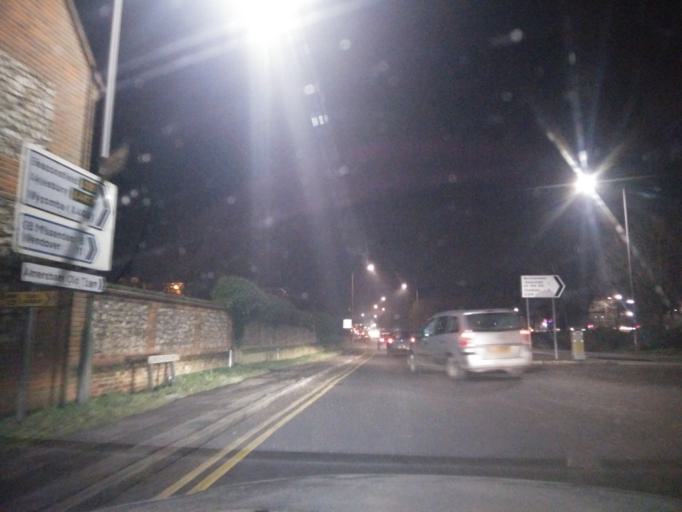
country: GB
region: England
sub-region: Buckinghamshire
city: Amersham
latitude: 51.6647
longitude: -0.6084
